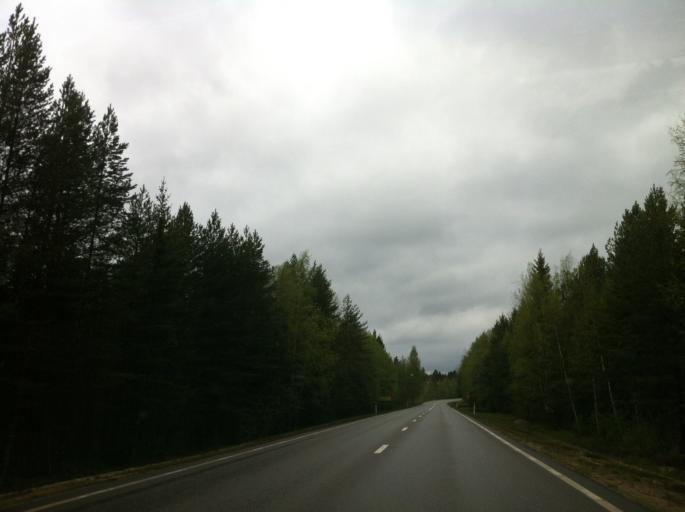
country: SE
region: Jaemtland
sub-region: Harjedalens Kommun
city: Sveg
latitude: 62.0617
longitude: 14.2834
